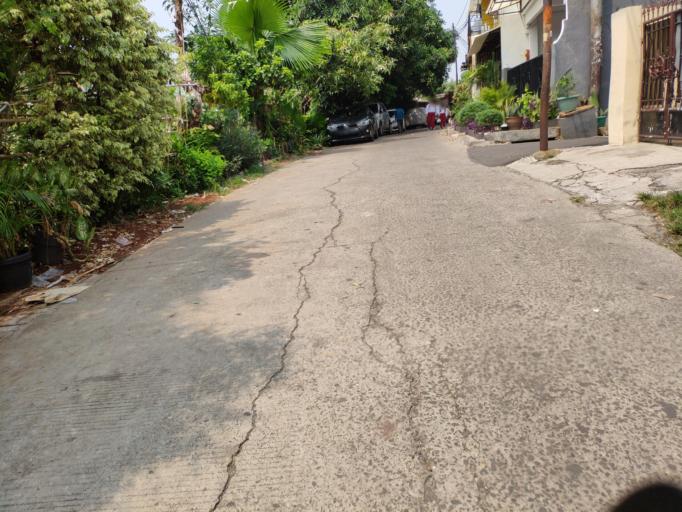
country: ID
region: Jakarta Raya
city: Jakarta
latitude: -6.2063
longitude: 106.8603
